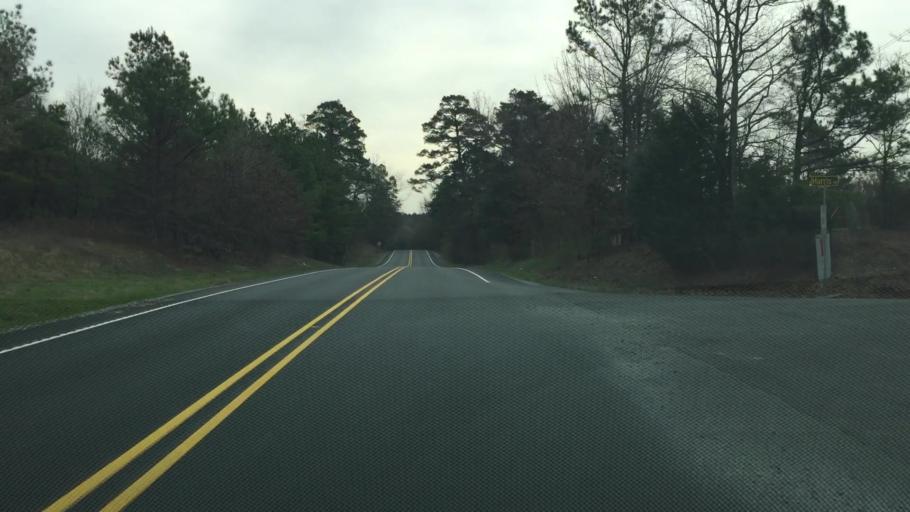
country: US
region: Arkansas
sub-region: Saline County
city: Haskell
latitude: 34.6122
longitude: -92.8057
